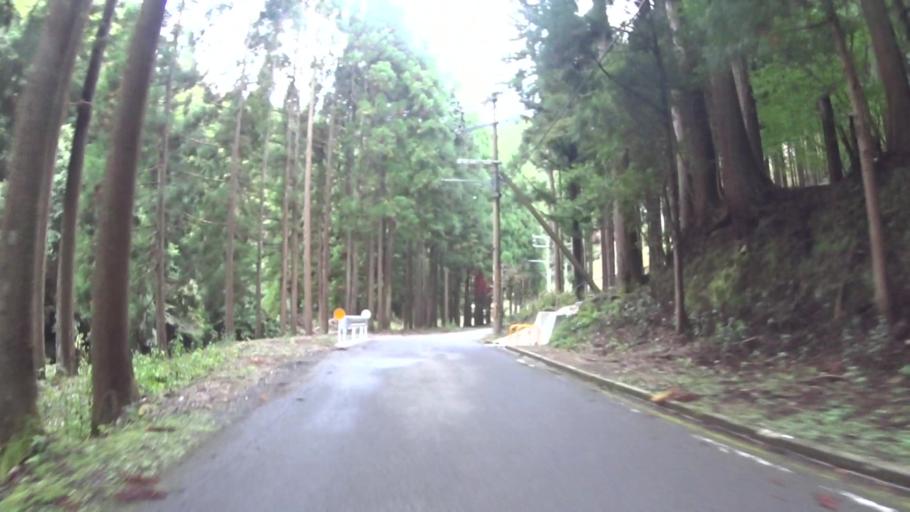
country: JP
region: Fukui
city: Obama
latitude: 35.2962
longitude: 135.6968
